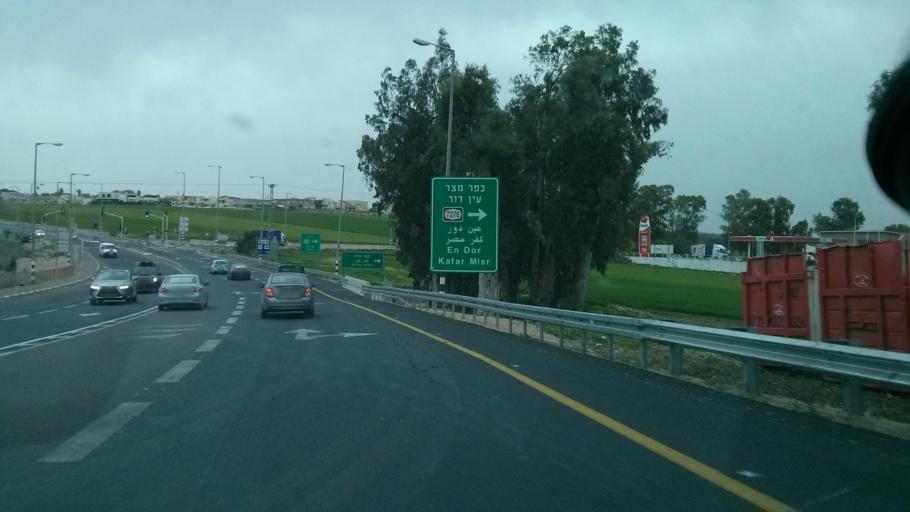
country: IL
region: Northern District
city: Kefar Tavor
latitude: 32.6781
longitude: 35.4111
